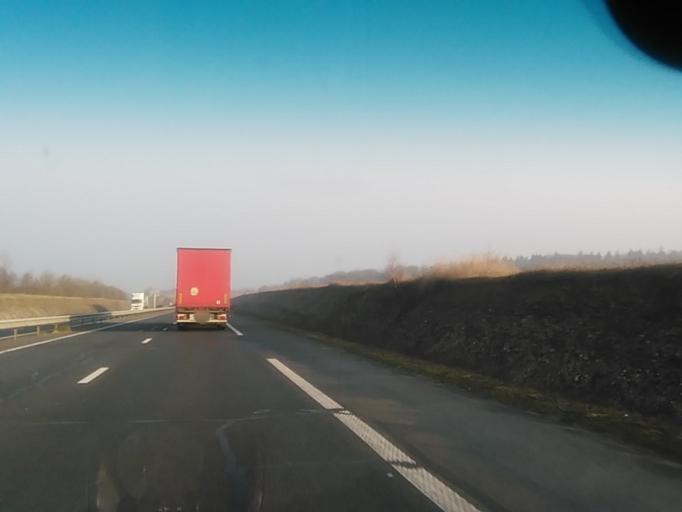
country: FR
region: Lower Normandy
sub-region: Departement du Calvados
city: Potigny
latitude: 48.9902
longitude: -0.2520
